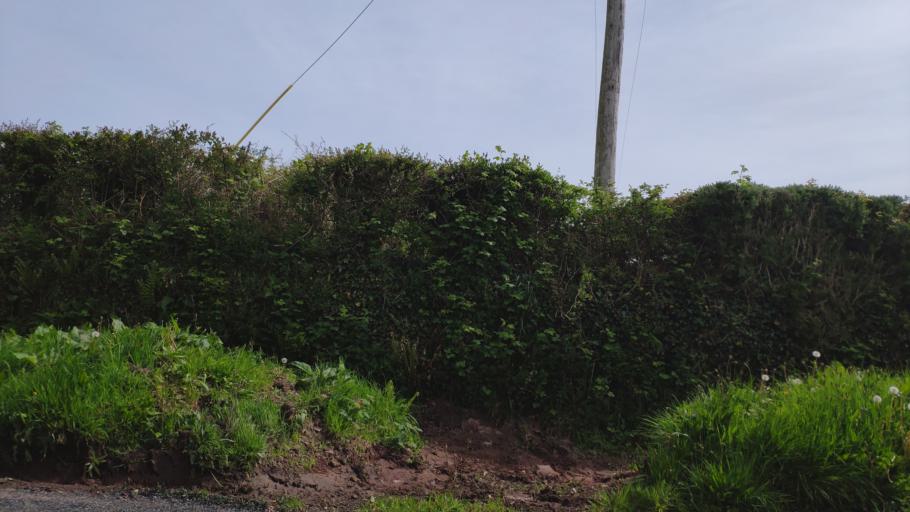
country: IE
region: Munster
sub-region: County Cork
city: Blarney
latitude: 51.9573
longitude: -8.5095
